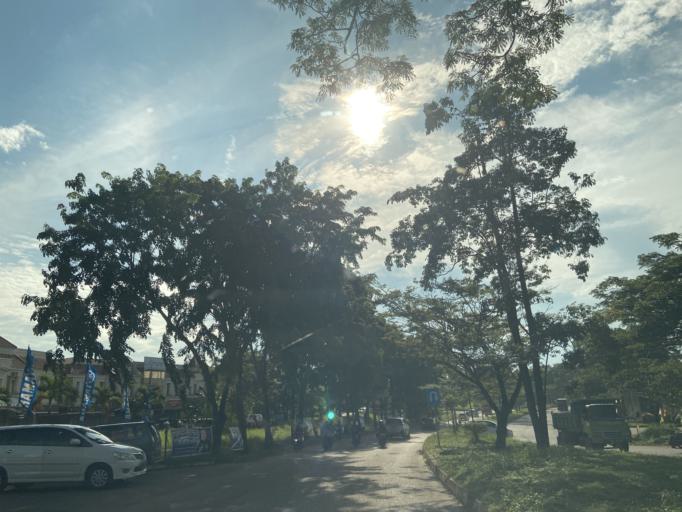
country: SG
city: Singapore
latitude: 1.1045
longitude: 104.0679
